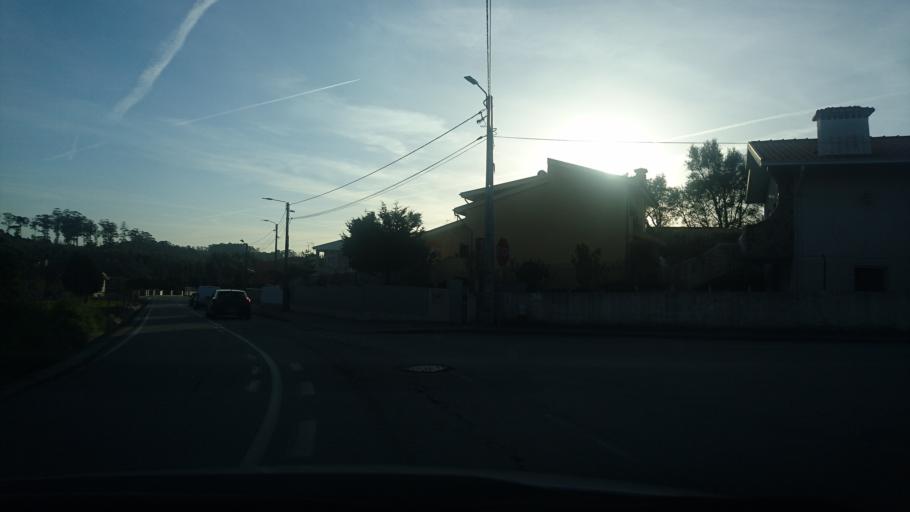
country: PT
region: Aveiro
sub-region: Santa Maria da Feira
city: Pacos de Brandao
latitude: 40.9823
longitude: -8.5977
